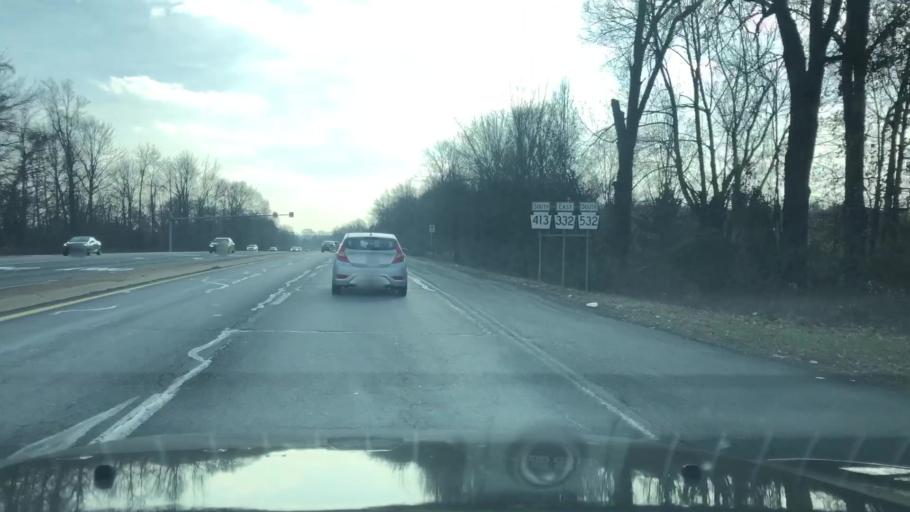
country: US
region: Pennsylvania
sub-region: Bucks County
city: Newtown
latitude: 40.2262
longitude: -74.9477
